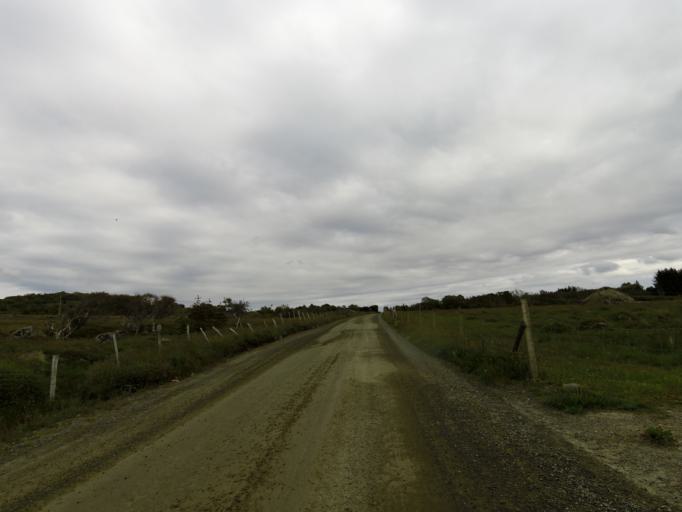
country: NO
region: Vest-Agder
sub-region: Farsund
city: Vestbygd
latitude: 58.1323
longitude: 6.6094
